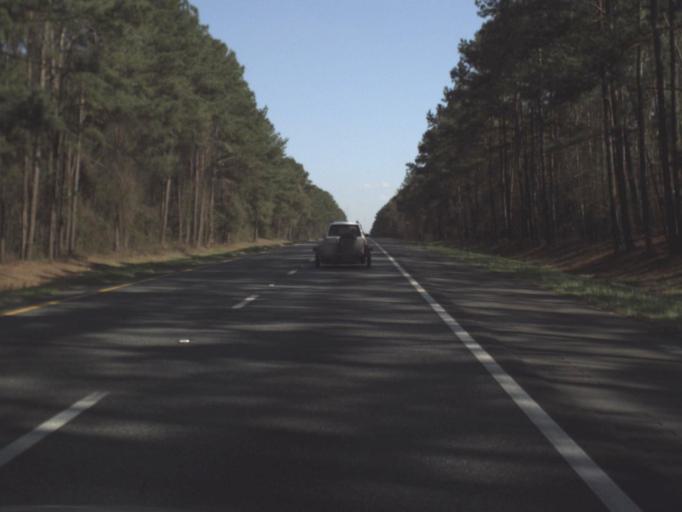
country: US
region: Florida
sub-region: Gadsden County
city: Midway
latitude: 30.5163
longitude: -84.4815
